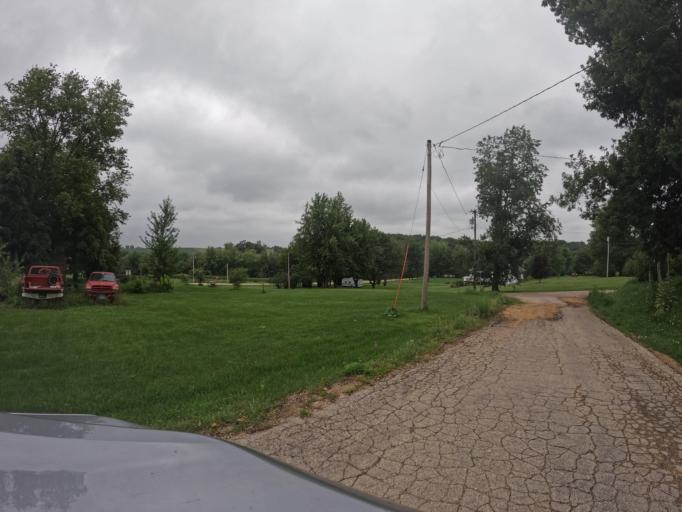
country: US
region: Iowa
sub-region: Clinton County
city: De Witt
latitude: 41.9135
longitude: -90.6042
